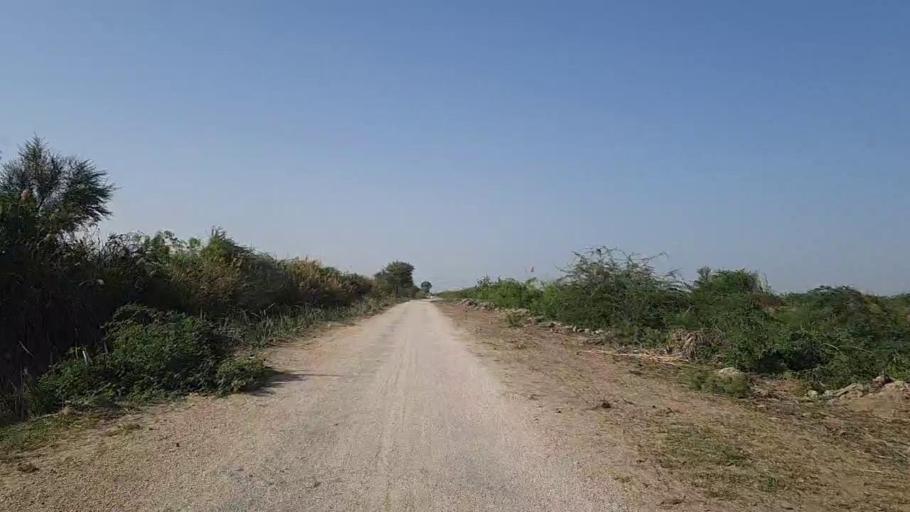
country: PK
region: Sindh
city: Kotri
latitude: 25.1429
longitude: 68.2659
